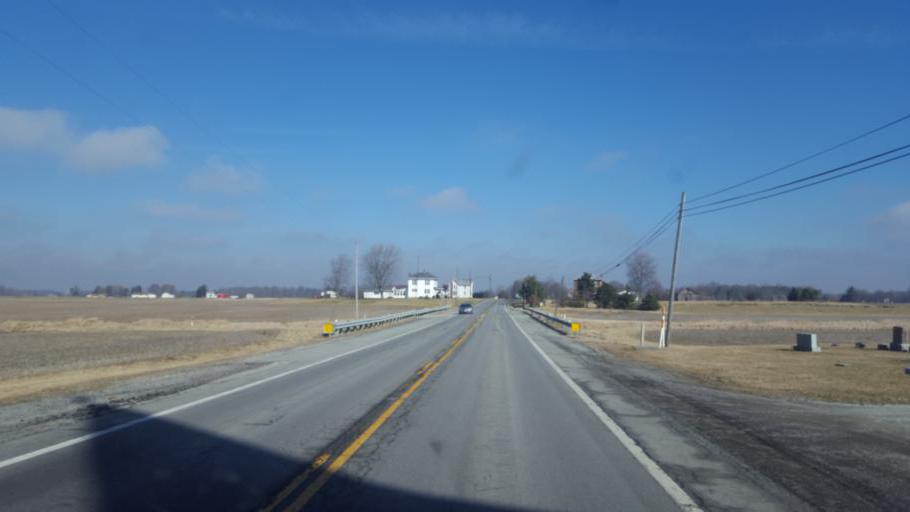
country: US
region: Ohio
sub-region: Crawford County
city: Bucyrus
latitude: 40.9437
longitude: -82.9466
